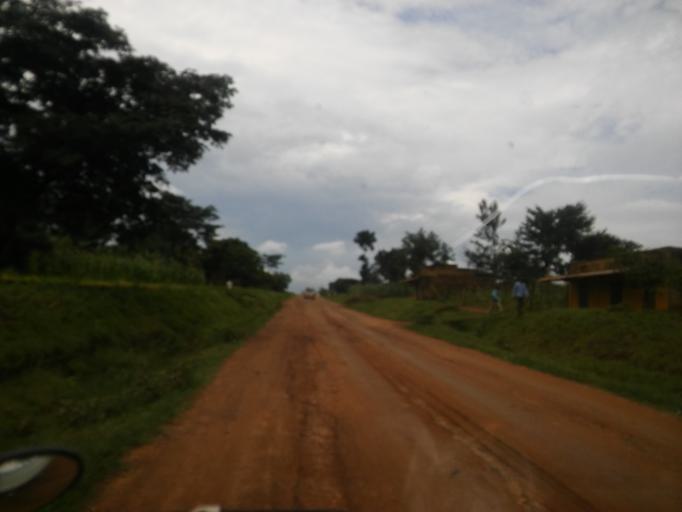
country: UG
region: Eastern Region
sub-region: Bududa District
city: Bududa
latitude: 0.9493
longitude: 34.2529
